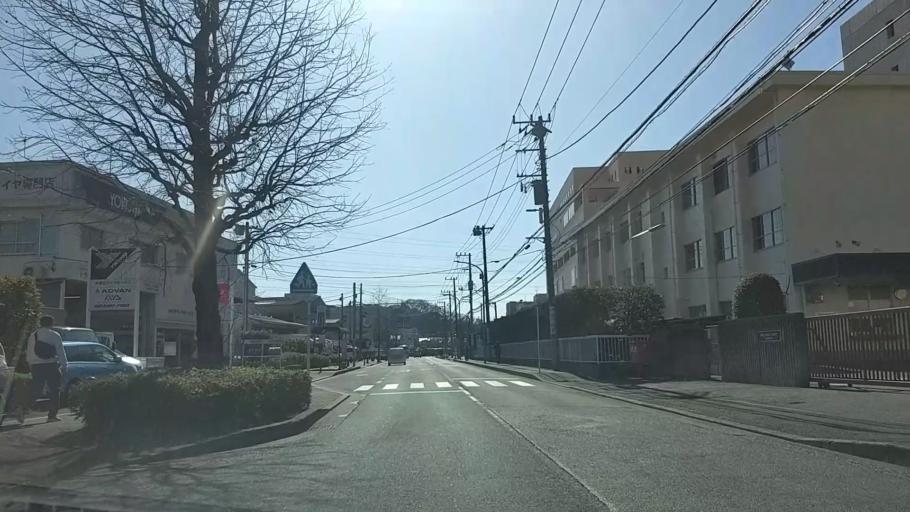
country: JP
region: Kanagawa
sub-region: Kawasaki-shi
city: Kawasaki
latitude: 35.5272
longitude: 139.6469
